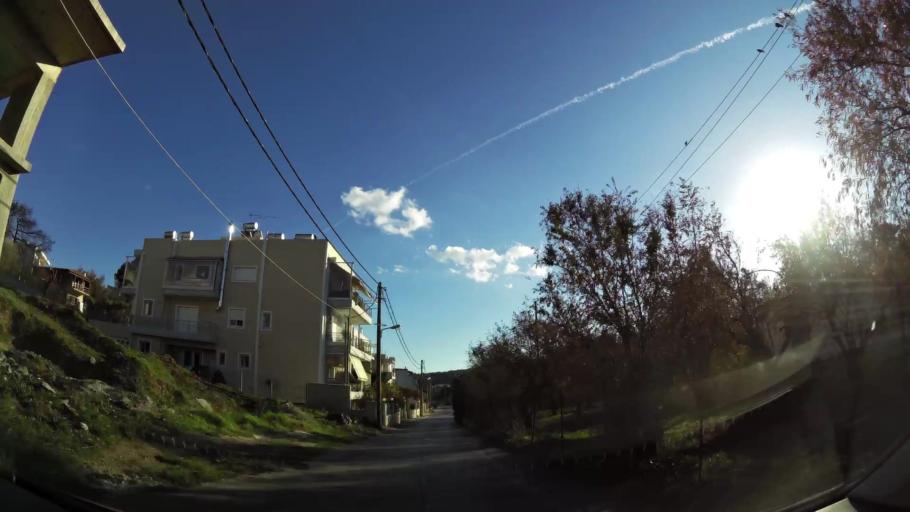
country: GR
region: Attica
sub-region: Nomarchia Anatolikis Attikis
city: Rafina
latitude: 38.0249
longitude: 23.9969
